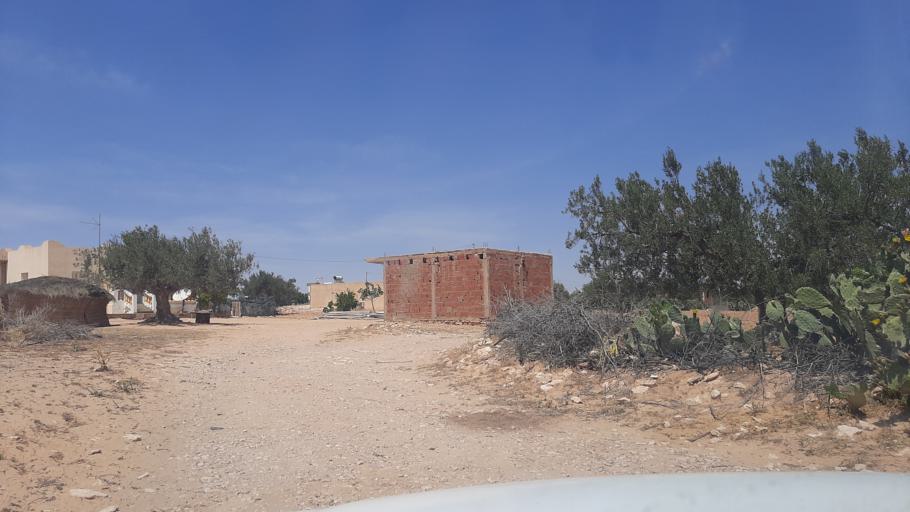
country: TN
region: Safaqis
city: Bi'r `Ali Bin Khalifah
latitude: 34.5669
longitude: 10.3469
